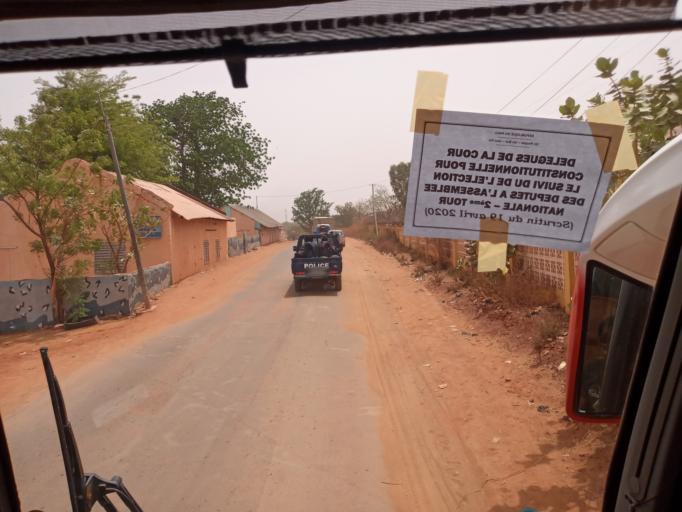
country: ML
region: Koulikoro
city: Koulikoro
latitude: 12.8815
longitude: -7.5439
